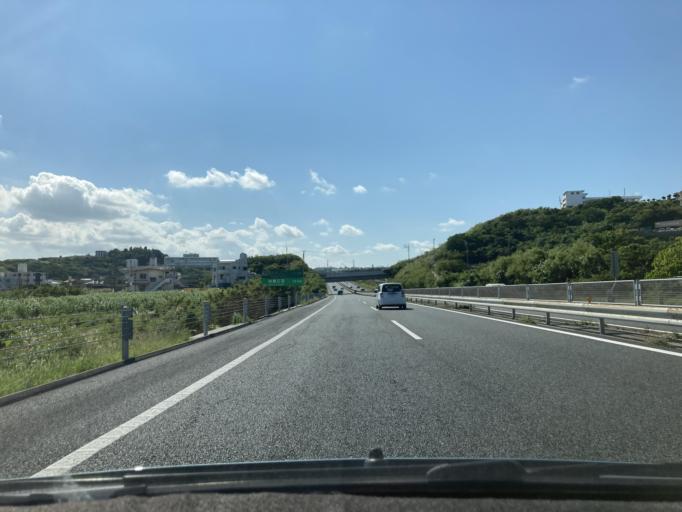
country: JP
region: Okinawa
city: Ginowan
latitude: 26.2365
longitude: 127.7408
